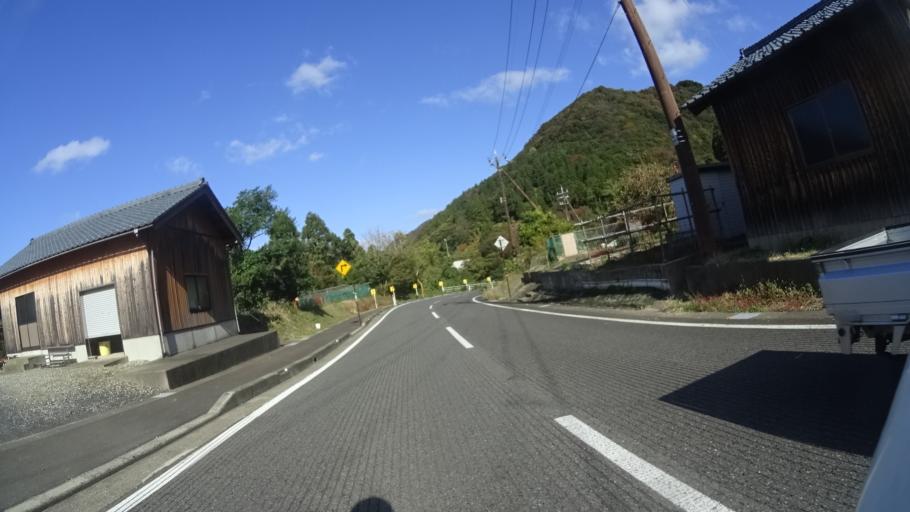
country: JP
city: Asahi
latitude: 35.9350
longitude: 136.0001
